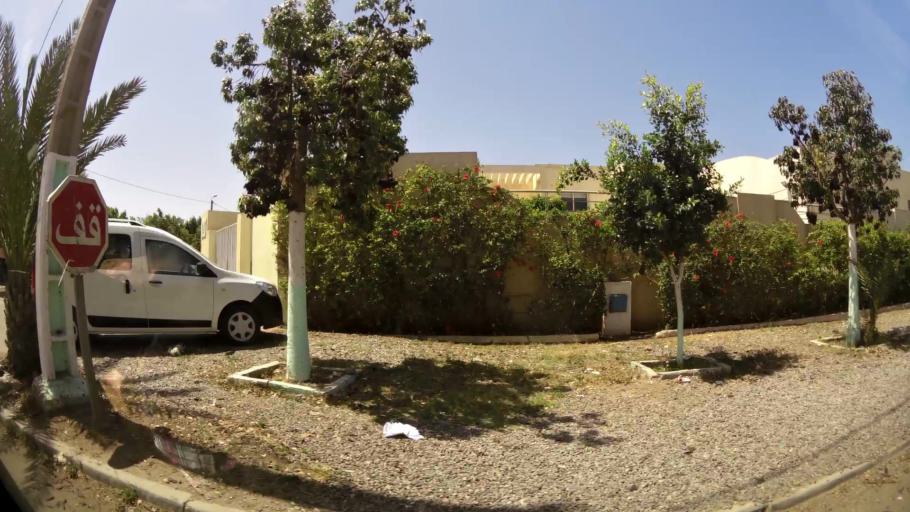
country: MA
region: Souss-Massa-Draa
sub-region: Inezgane-Ait Mellou
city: Inezgane
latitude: 30.3393
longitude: -9.4846
